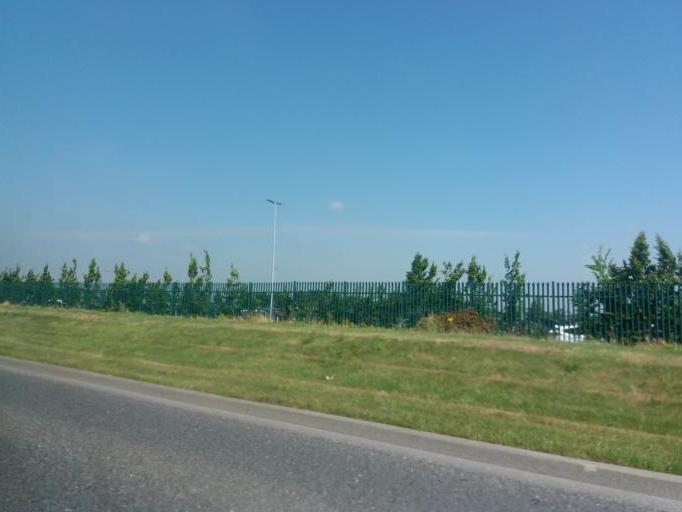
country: IE
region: Leinster
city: Ballymun
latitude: 53.4177
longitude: -6.2696
